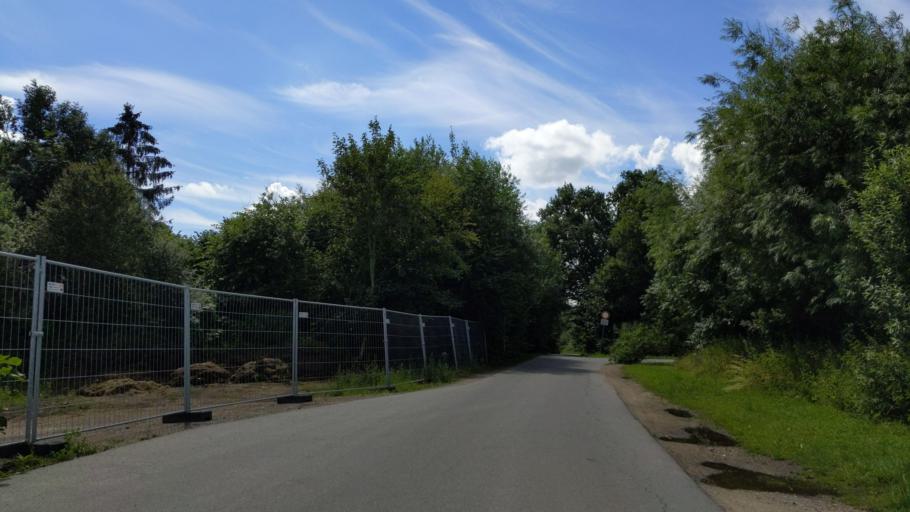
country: DE
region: Mecklenburg-Vorpommern
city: Dassow
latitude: 53.9048
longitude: 10.9797
